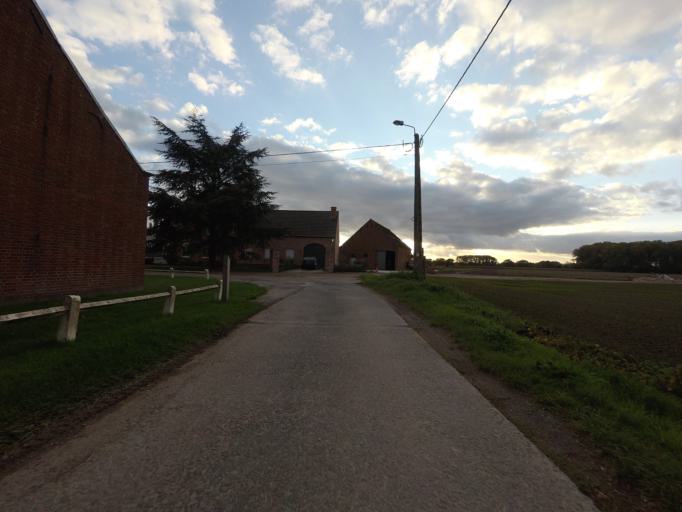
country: BE
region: Flanders
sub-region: Provincie Vlaams-Brabant
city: Kapelle-op-den-Bos
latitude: 51.0357
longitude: 4.3791
